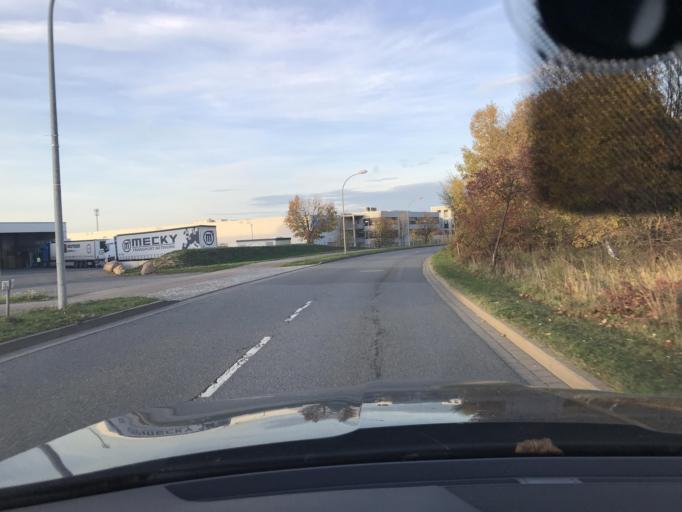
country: DE
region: Saxony-Anhalt
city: Ilsenburg
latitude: 51.8735
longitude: 10.6929
